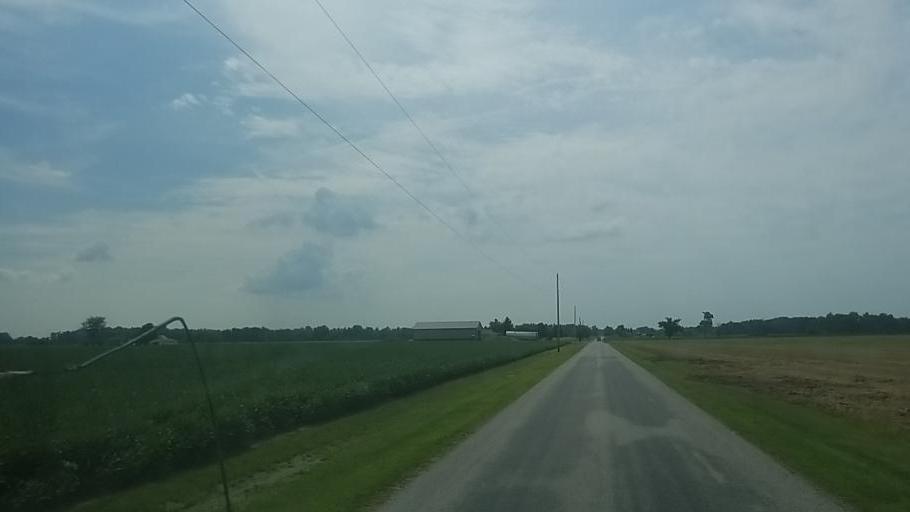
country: US
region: Ohio
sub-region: Hardin County
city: Forest
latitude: 40.7600
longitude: -83.5527
